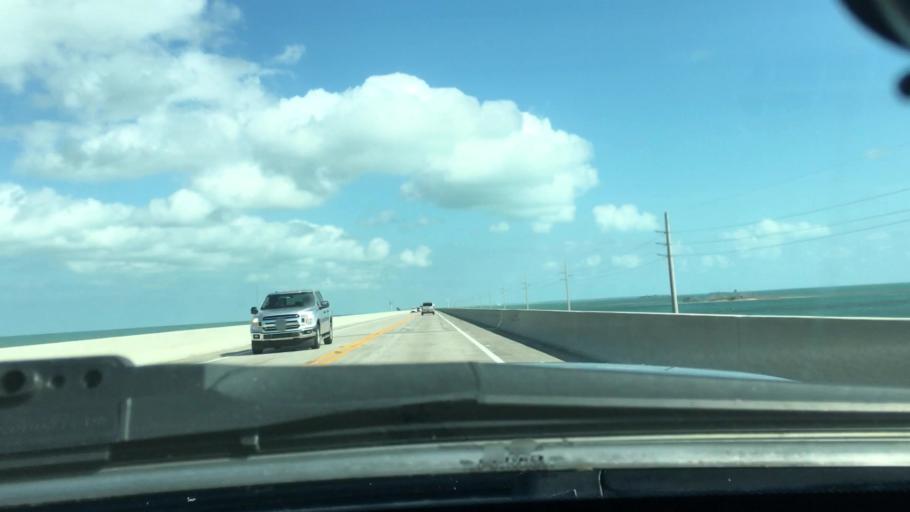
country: US
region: Florida
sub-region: Monroe County
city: Big Pine Key
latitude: 24.6838
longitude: -81.2236
